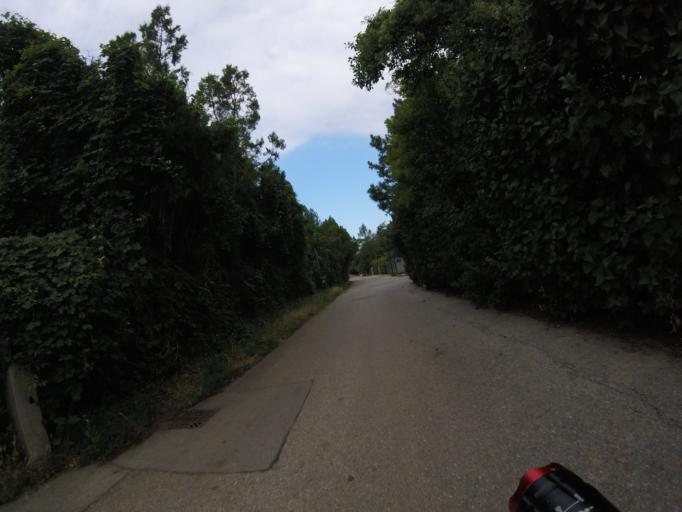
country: AT
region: Lower Austria
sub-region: Politischer Bezirk Modling
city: Modling
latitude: 48.0741
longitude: 16.3000
